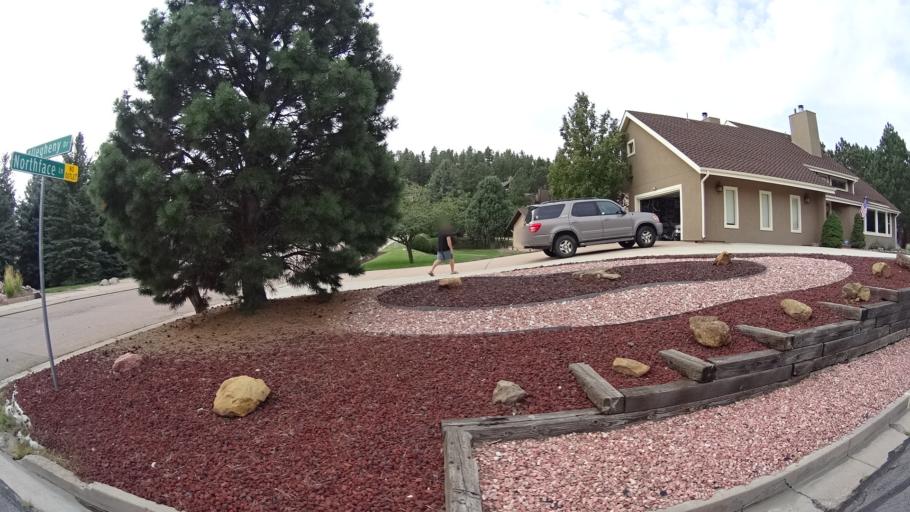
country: US
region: Colorado
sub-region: El Paso County
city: Air Force Academy
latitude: 38.9294
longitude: -104.8528
